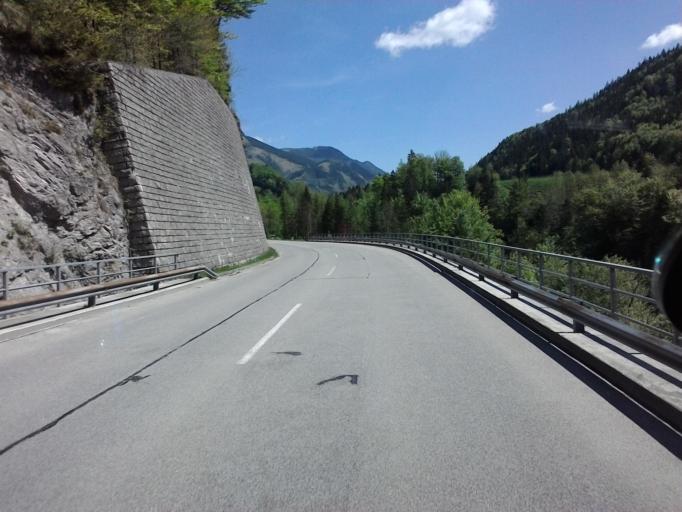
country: AT
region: Styria
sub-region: Politischer Bezirk Liezen
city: Gams bei Hieflau
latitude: 47.6906
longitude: 14.7770
